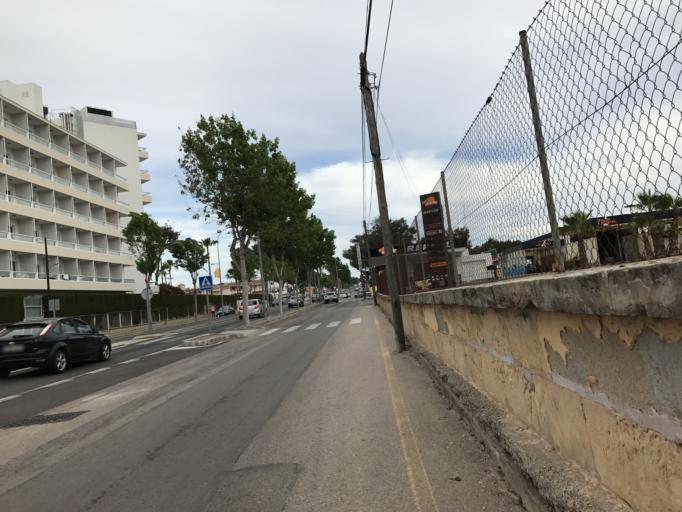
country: ES
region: Balearic Islands
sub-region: Illes Balears
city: Santa Margalida
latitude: 39.7637
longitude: 3.1502
